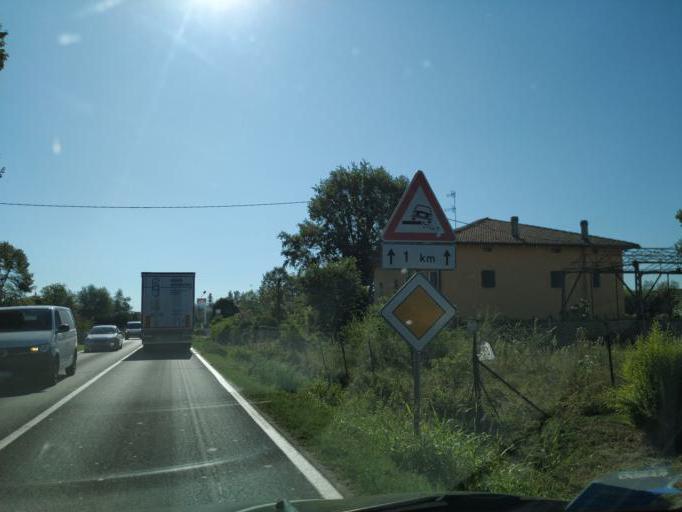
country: IT
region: Emilia-Romagna
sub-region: Provincia di Bologna
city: Sant'Agata Bolognese
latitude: 44.6570
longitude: 11.1343
